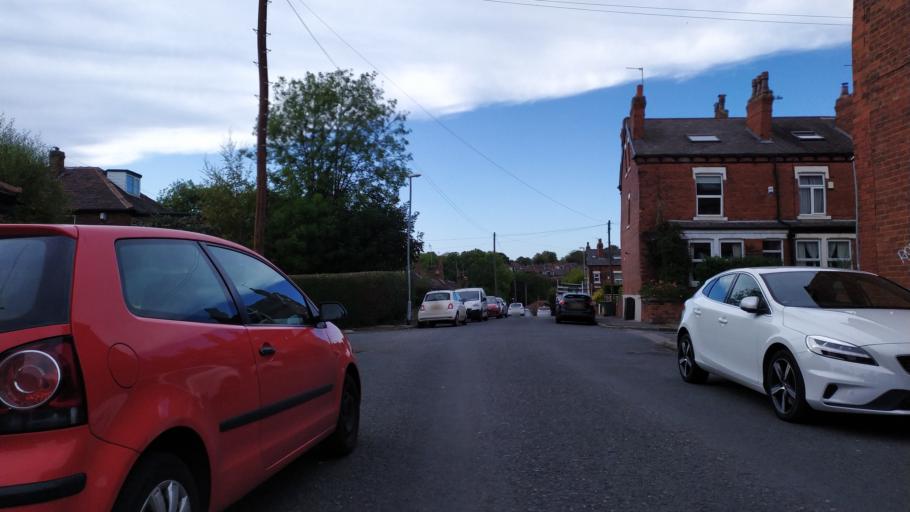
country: GB
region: England
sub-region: City and Borough of Leeds
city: Chapel Allerton
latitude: 53.8256
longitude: -1.5663
